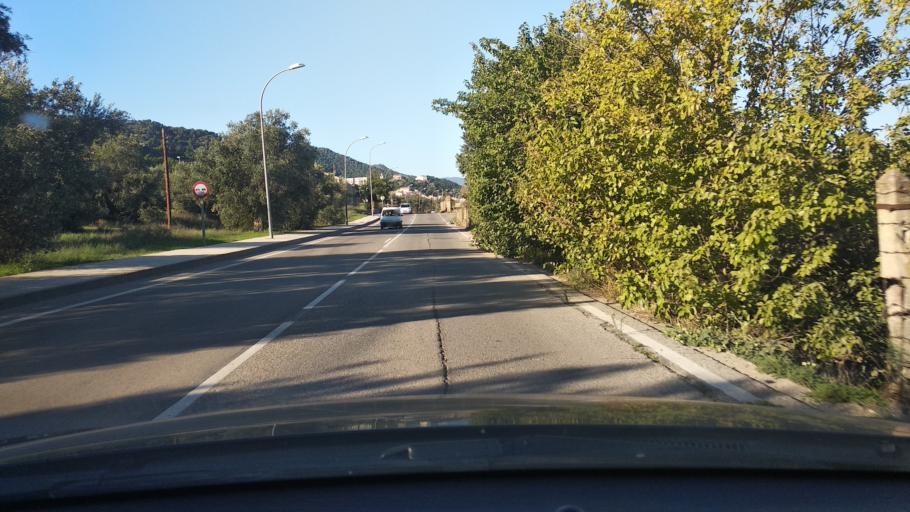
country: ES
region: Murcia
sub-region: Murcia
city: Murcia
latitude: 37.9490
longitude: -1.1031
